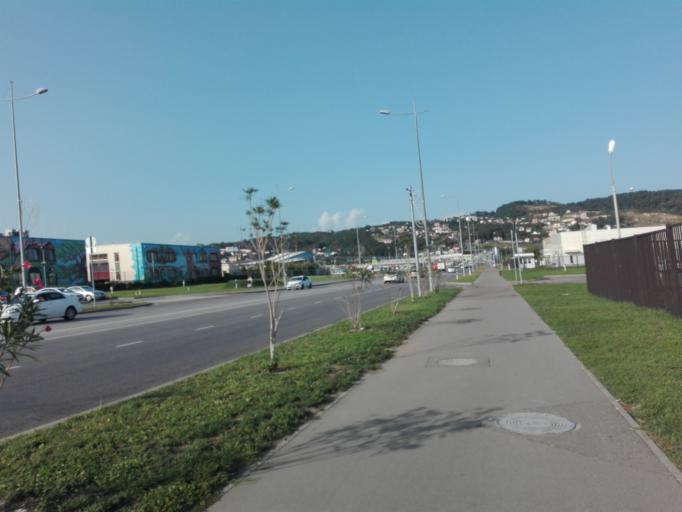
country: RU
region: Krasnodarskiy
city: Adler
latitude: 43.4040
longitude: 39.9713
